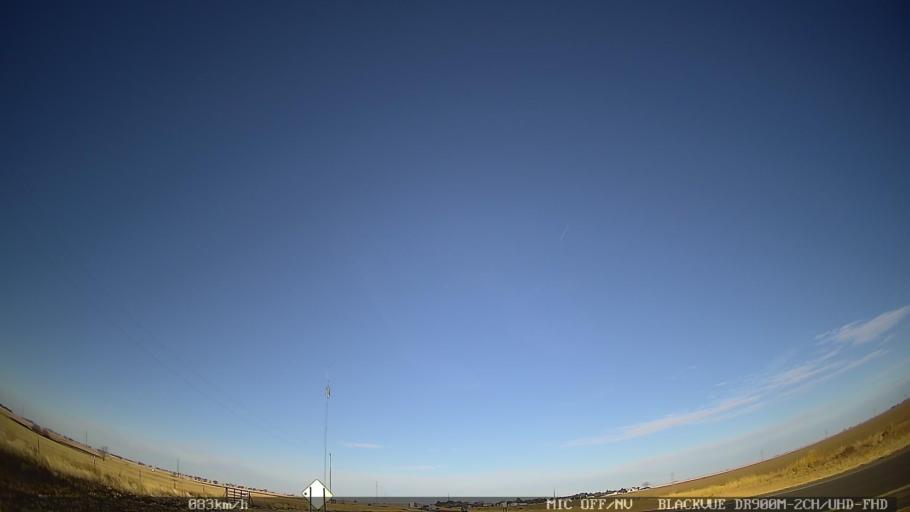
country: US
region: New Mexico
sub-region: Curry County
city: Clovis
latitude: 34.4340
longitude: -103.2437
